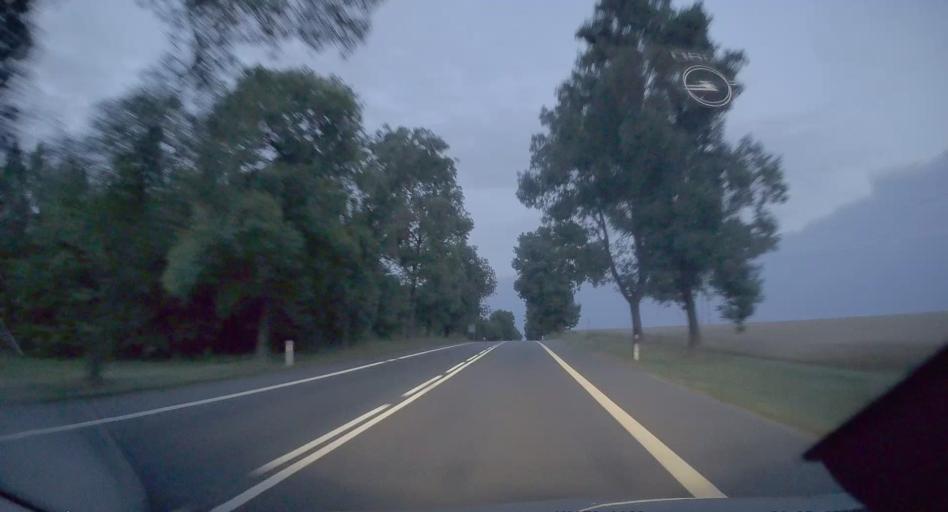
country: PL
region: Silesian Voivodeship
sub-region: Powiat klobucki
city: Klobuck
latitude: 50.9105
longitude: 18.9077
